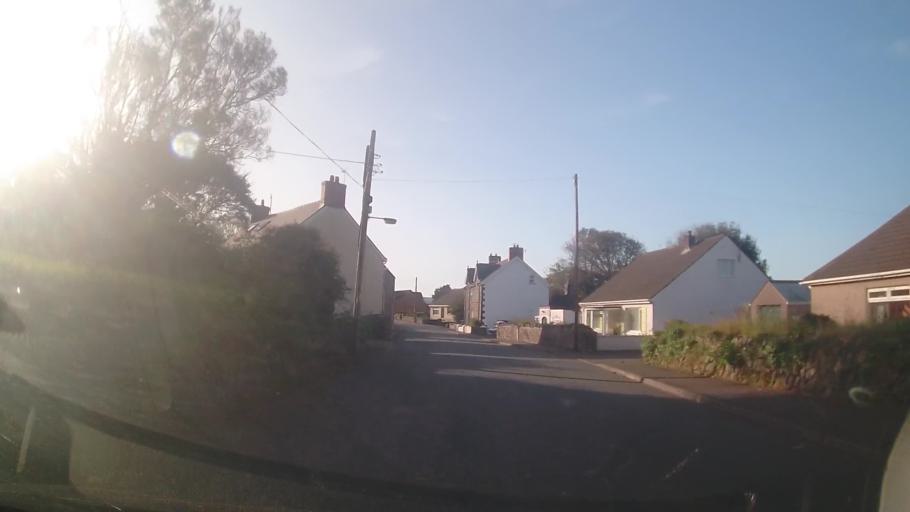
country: GB
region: Wales
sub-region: Pembrokeshire
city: Fishguard
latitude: 51.9914
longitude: -4.9691
